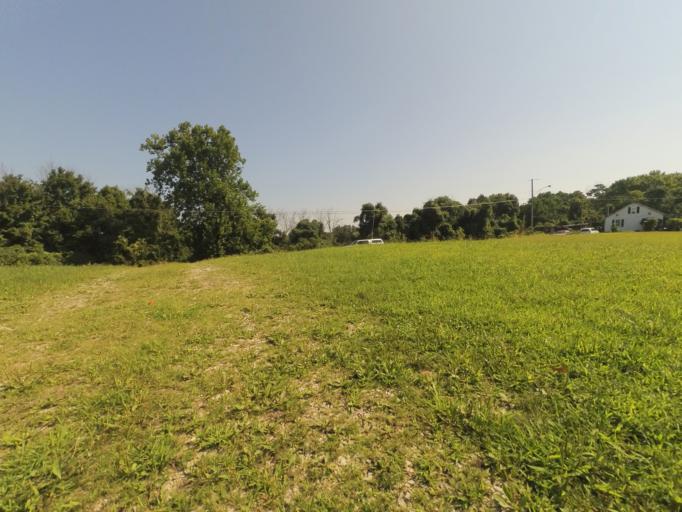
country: US
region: West Virginia
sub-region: Cabell County
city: Huntington
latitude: 38.4372
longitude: -82.4414
